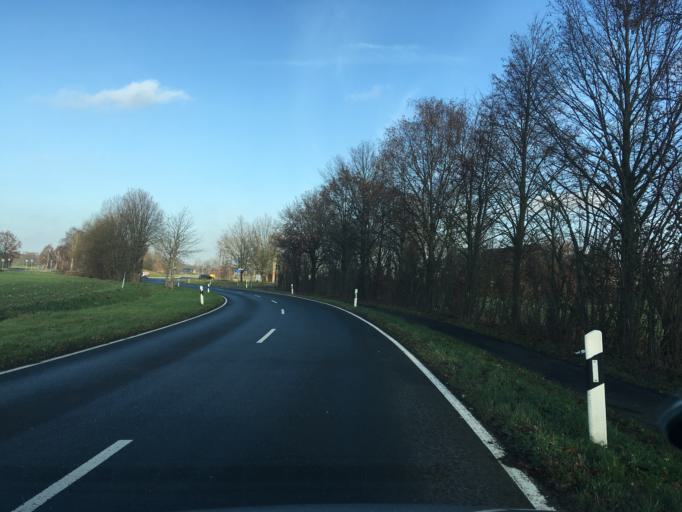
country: DE
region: North Rhine-Westphalia
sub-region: Regierungsbezirk Munster
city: Gescher
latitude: 51.9388
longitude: 6.9843
